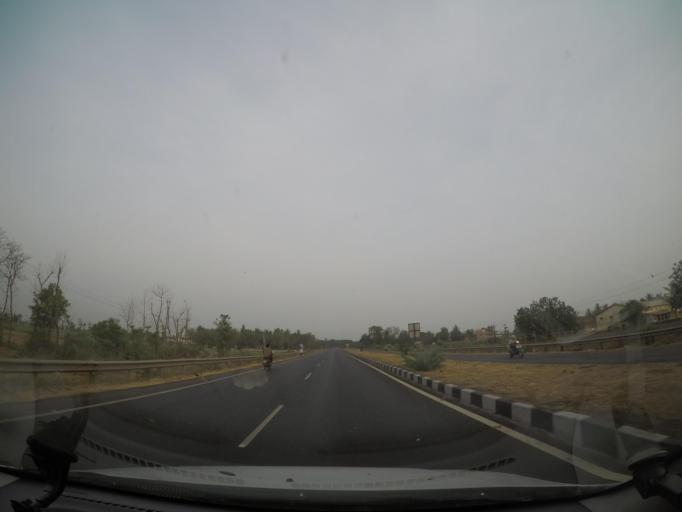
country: IN
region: Andhra Pradesh
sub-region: Krishna
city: Gannavaram
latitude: 16.6100
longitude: 80.9164
